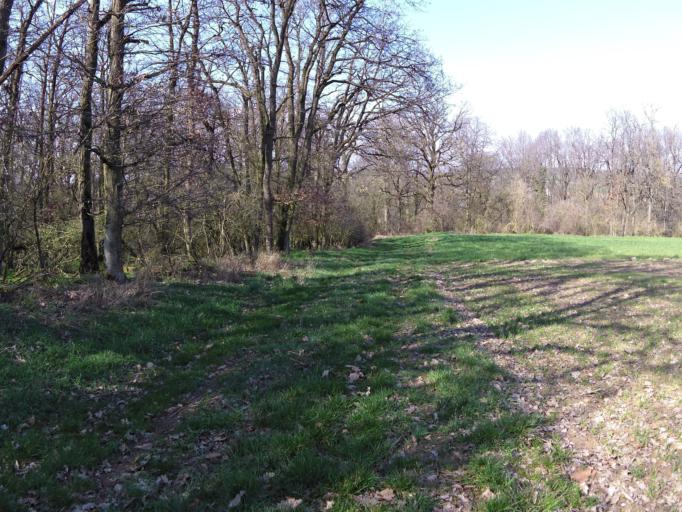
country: DE
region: Bavaria
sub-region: Regierungsbezirk Unterfranken
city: Rottendorf
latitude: 49.8046
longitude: 10.0587
